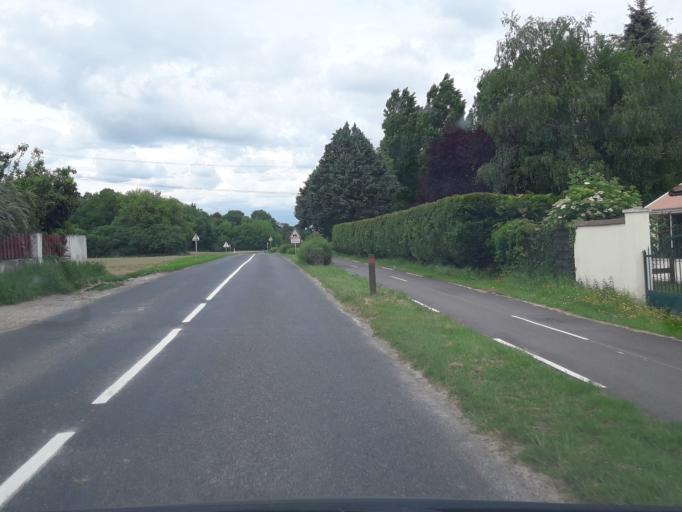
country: FR
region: Ile-de-France
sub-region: Departement de l'Essonne
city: Boissy-le-Cutte
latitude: 48.4487
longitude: 2.3057
